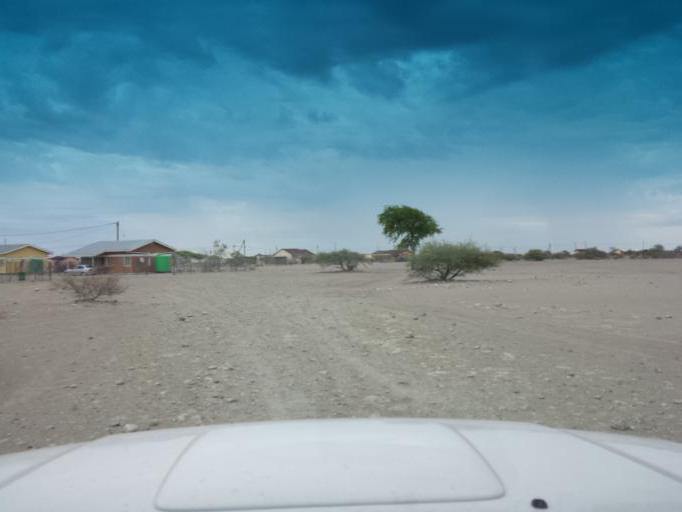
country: BW
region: Central
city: Mopipi
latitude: -21.2019
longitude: 24.8595
